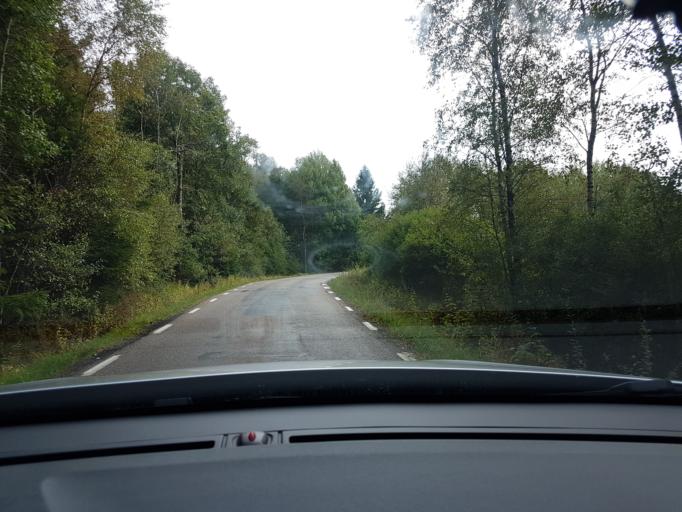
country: SE
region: Vaestra Goetaland
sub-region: Ale Kommun
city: Skepplanda
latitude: 57.8986
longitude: 12.1932
